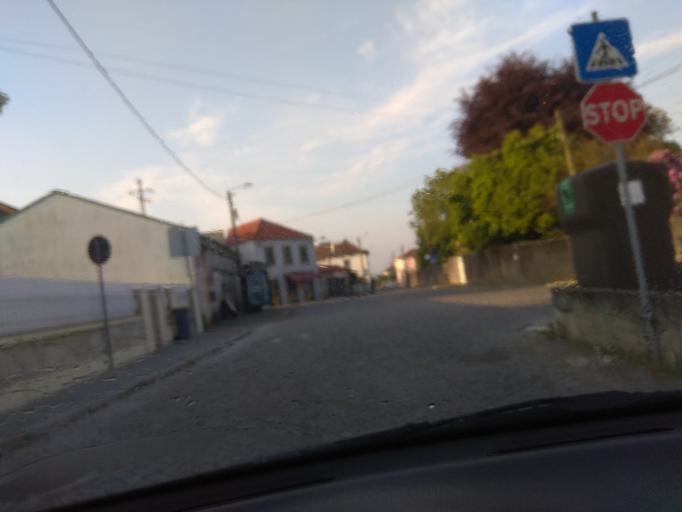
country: PT
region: Porto
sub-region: Maia
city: Nogueira
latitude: 41.2567
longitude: -8.5915
